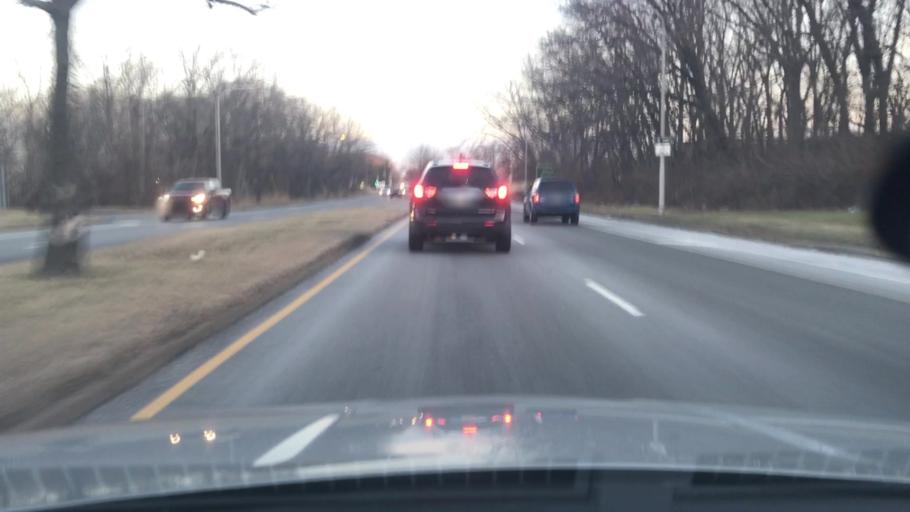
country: US
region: New Jersey
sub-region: Burlington County
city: Riverton
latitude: 40.0738
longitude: -75.0161
